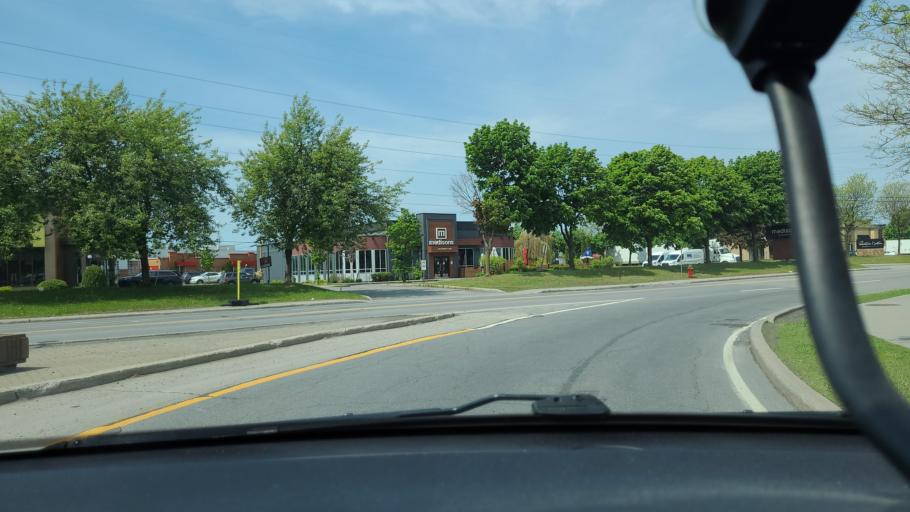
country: CA
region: Quebec
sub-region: Monteregie
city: Boucherville
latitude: 45.5688
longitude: -73.4442
